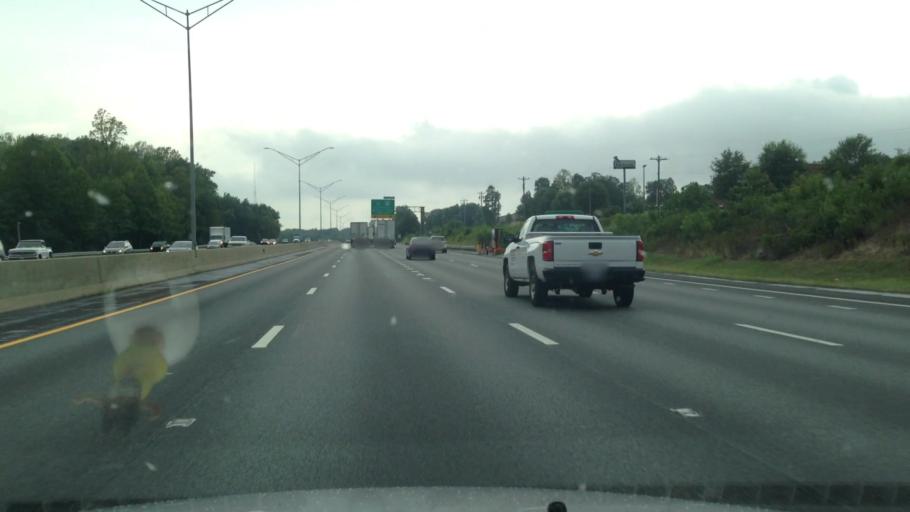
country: US
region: North Carolina
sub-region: Forsyth County
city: Kernersville
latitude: 36.0947
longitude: -80.0027
